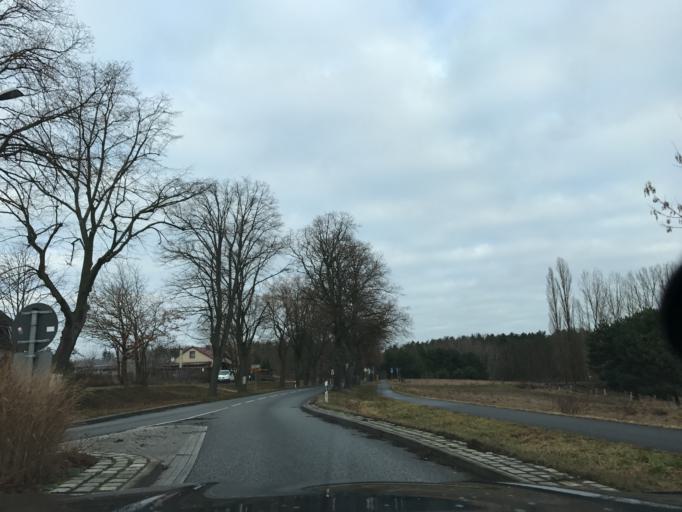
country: DE
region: Brandenburg
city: Gross Kreutz
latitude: 52.3236
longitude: 12.7333
